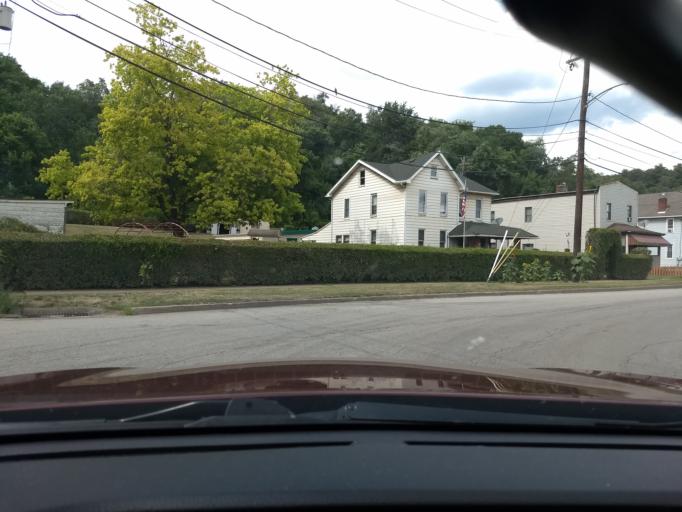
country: US
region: Pennsylvania
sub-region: Allegheny County
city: Brackenridge
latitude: 40.6169
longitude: -79.7225
